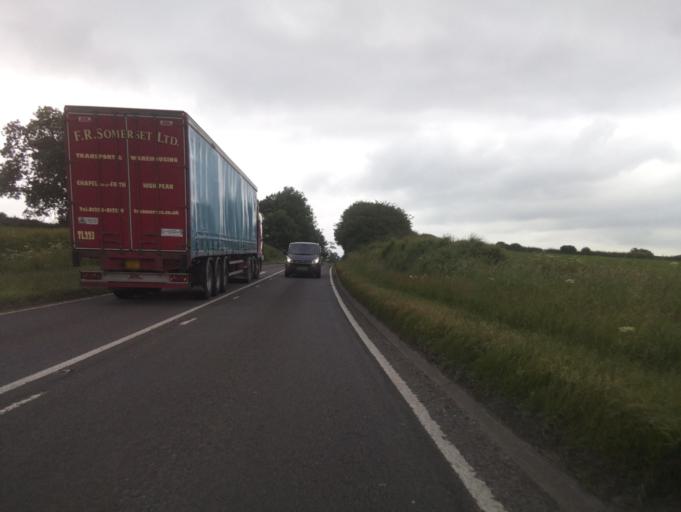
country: GB
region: England
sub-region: Staffordshire
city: Mayfield
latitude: 52.9382
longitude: -1.7621
